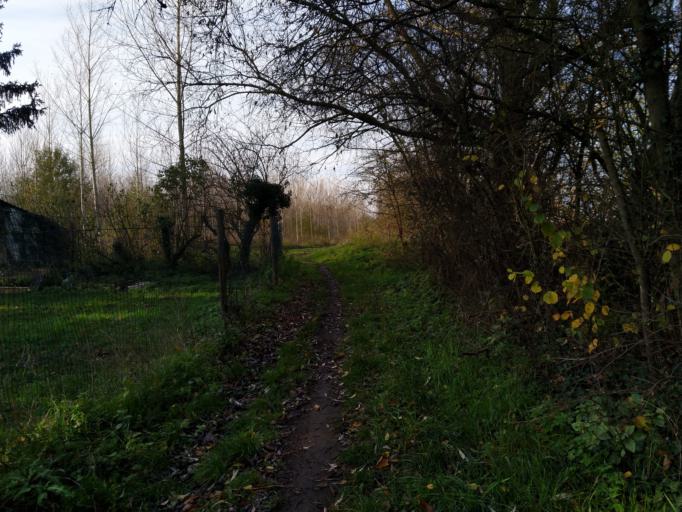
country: BE
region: Wallonia
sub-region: Province du Hainaut
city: Boussu
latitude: 50.4422
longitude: 3.7918
